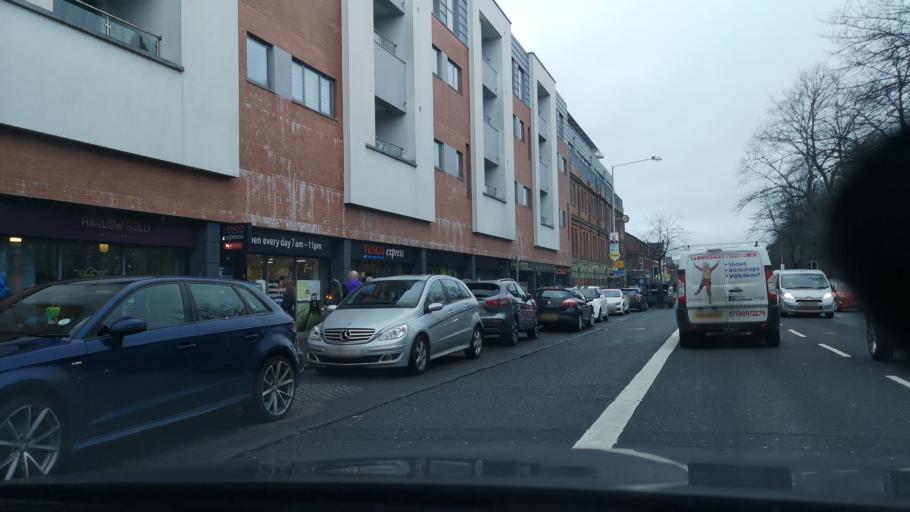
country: GB
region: Northern Ireland
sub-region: City of Belfast
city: Belfast
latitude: 54.5789
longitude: -5.9196
